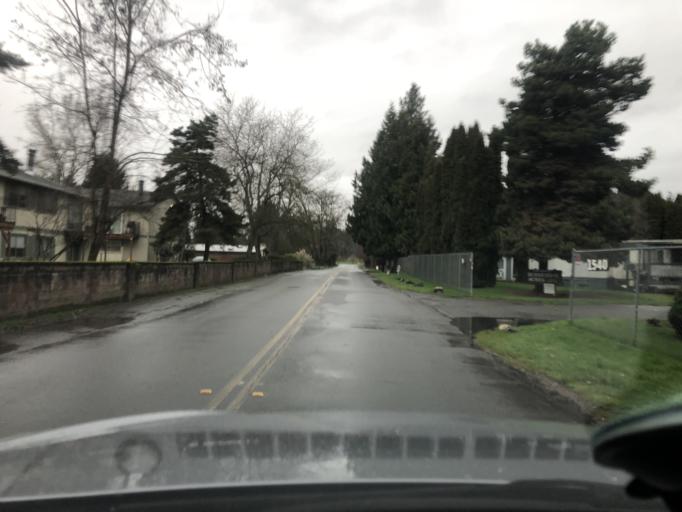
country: US
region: Washington
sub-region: King County
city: Kent
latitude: 47.3647
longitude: -122.2272
